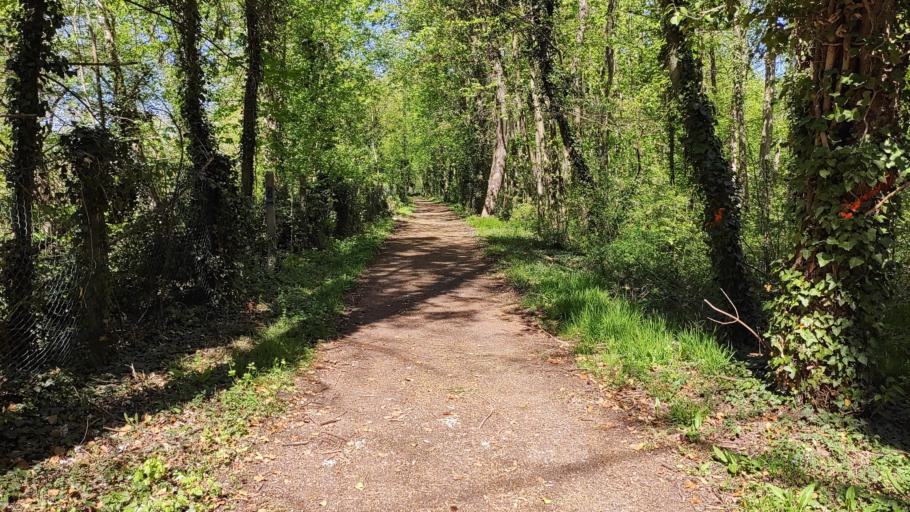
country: DE
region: Baden-Wuerttemberg
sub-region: Freiburg Region
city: Merdingen
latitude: 47.9955
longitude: 7.6599
